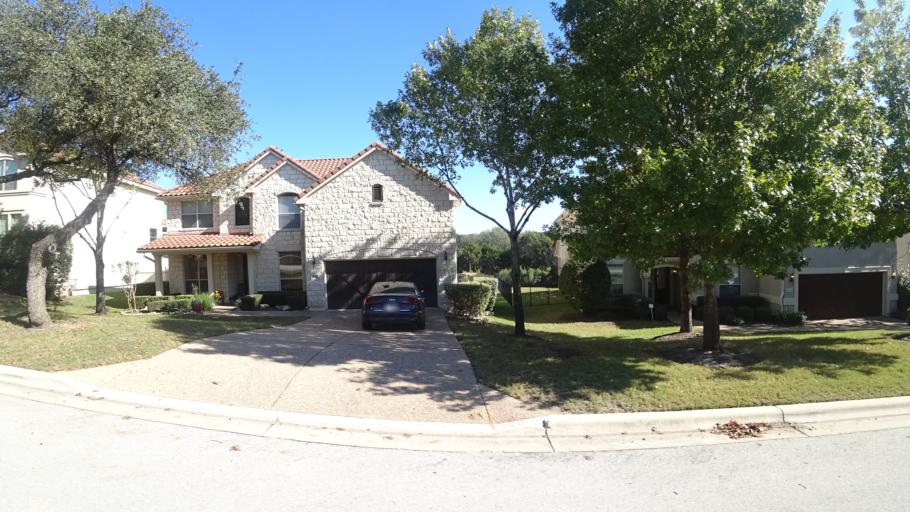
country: US
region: Texas
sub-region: Travis County
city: Hudson Bend
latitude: 30.3594
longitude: -97.8848
